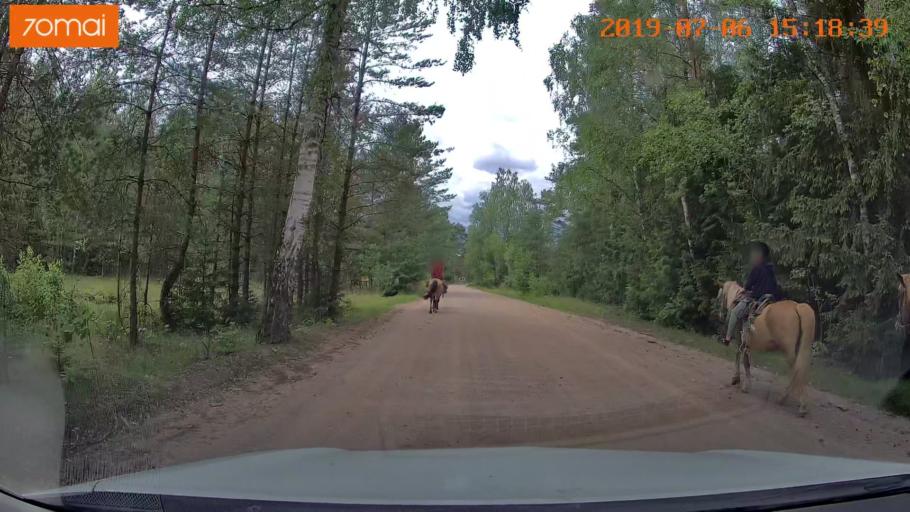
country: BY
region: Minsk
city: Ivyanyets
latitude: 53.9931
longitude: 26.6515
